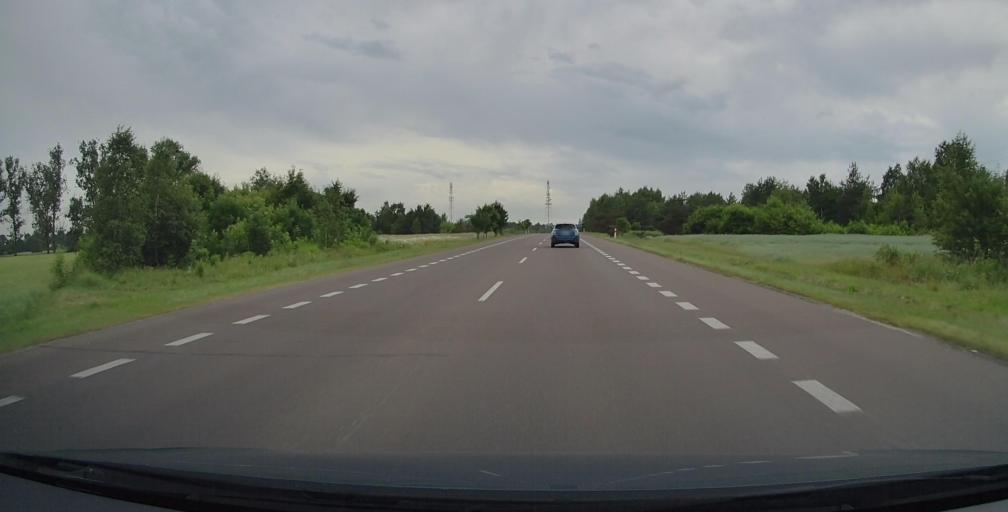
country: PL
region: Lublin Voivodeship
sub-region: Biala Podlaska
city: Biala Podlaska
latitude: 52.0393
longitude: 23.0818
